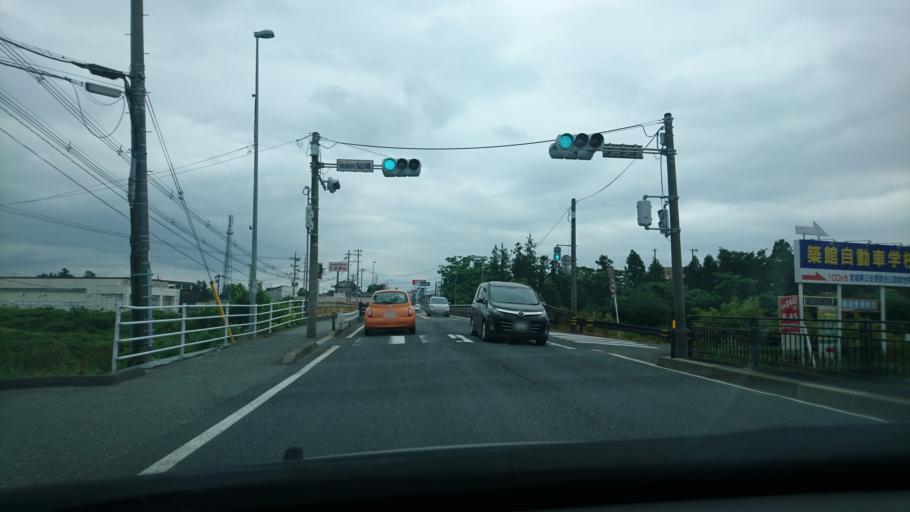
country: JP
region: Miyagi
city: Furukawa
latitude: 38.7416
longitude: 141.0178
